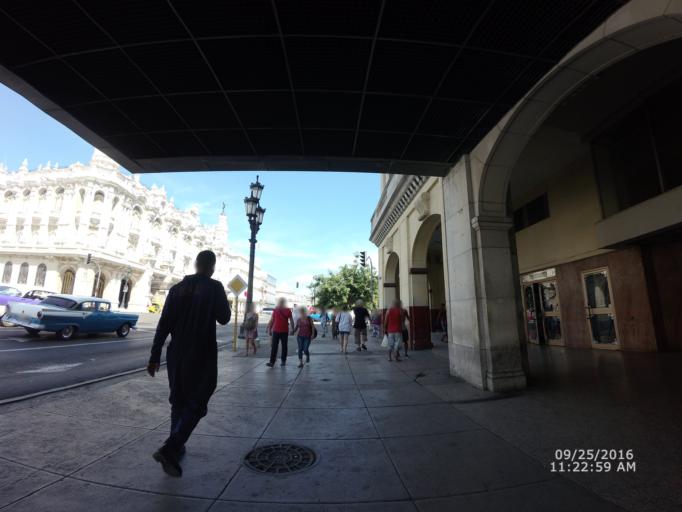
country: CU
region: La Habana
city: Centro Habana
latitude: 23.1363
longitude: -82.3585
